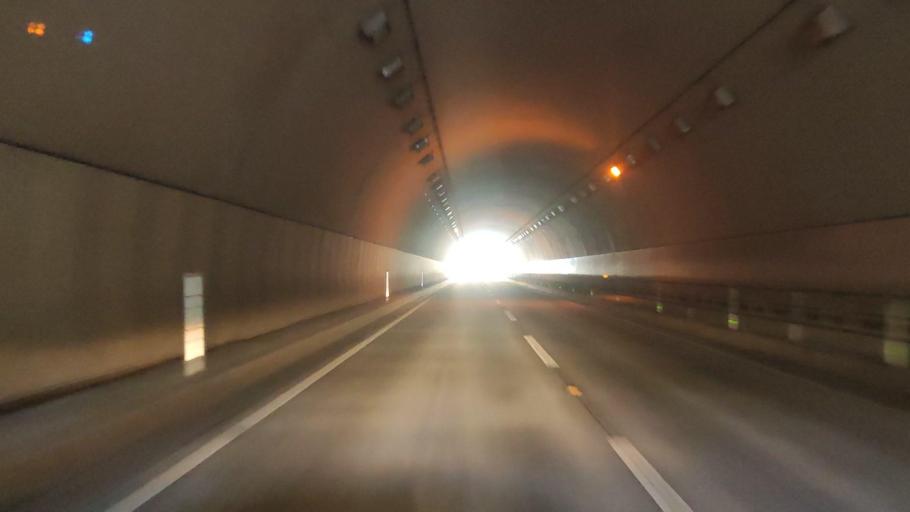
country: JP
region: Miyazaki
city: Nobeoka
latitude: 32.7022
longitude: 131.8154
